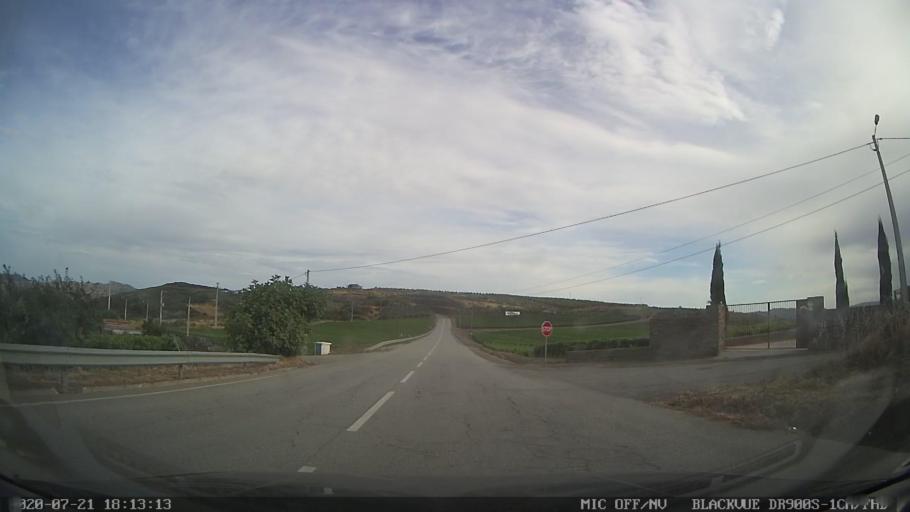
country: PT
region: Viseu
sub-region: Sao Joao da Pesqueira
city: Sao Joao da Pesqueira
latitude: 41.1327
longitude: -7.3984
